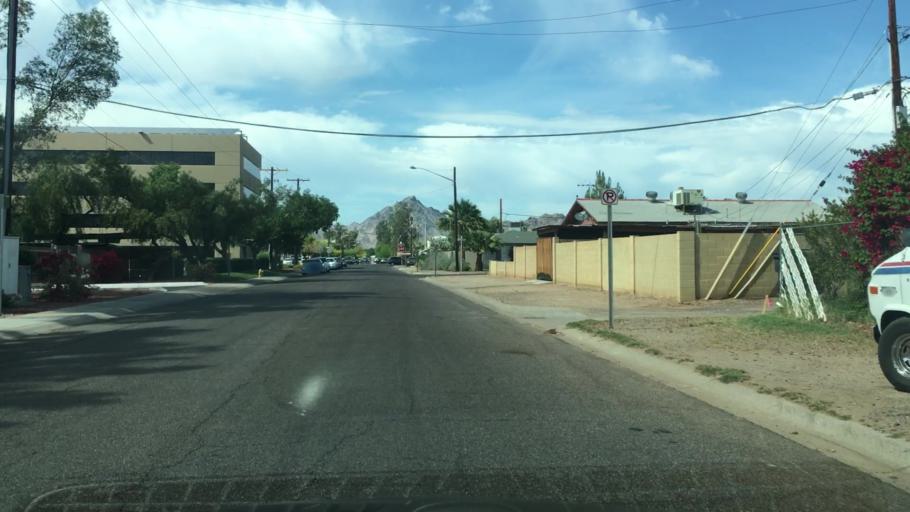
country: US
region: Arizona
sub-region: Maricopa County
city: Phoenix
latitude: 33.4935
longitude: -112.0238
